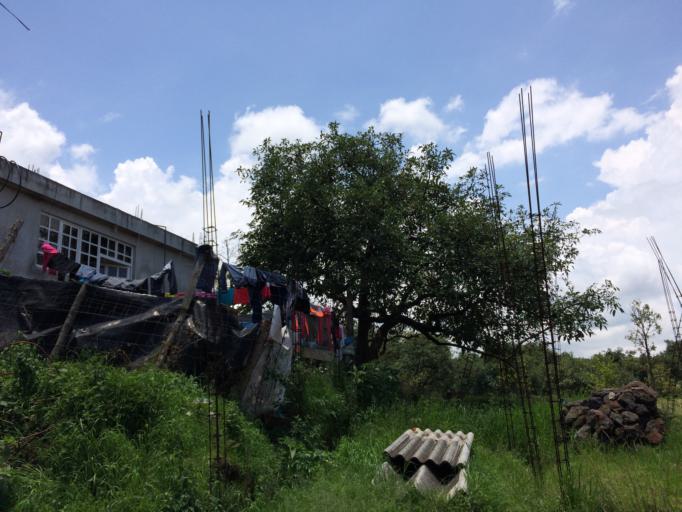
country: MX
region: Michoacan
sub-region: Periban
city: San Francisco Periban
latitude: 19.5560
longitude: -102.3969
